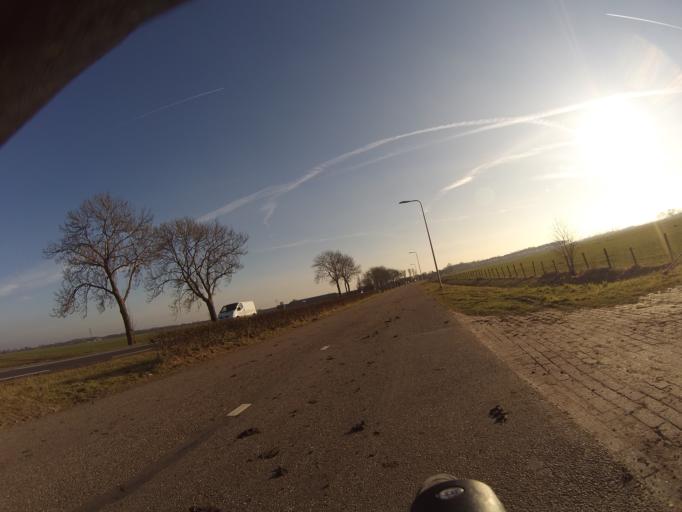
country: NL
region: Utrecht
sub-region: Gemeente Bunschoten
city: Bunschoten
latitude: 52.2177
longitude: 5.3669
